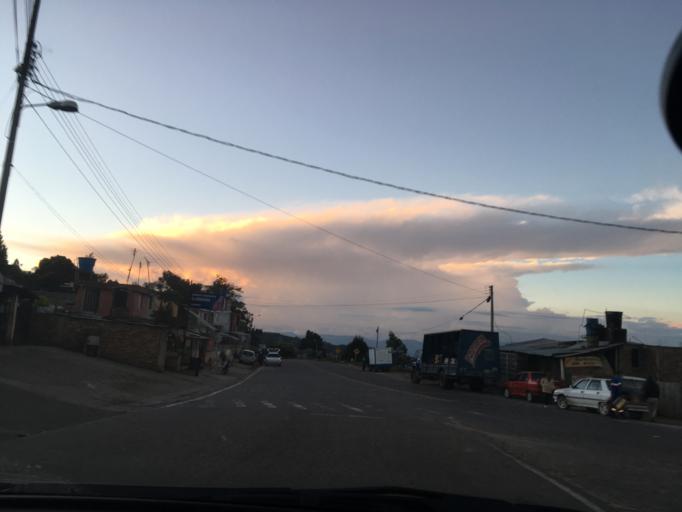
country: CO
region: Boyaca
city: Sogamoso
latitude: 5.6182
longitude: -72.9057
